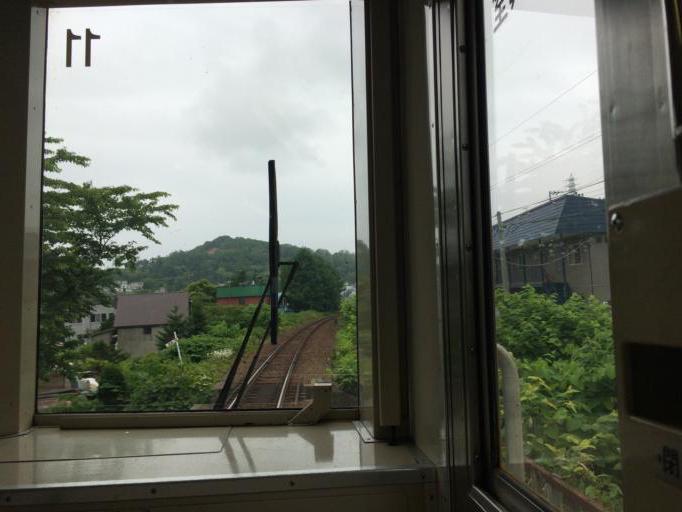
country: JP
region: Hokkaido
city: Otaru
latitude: 43.2079
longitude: 140.9776
